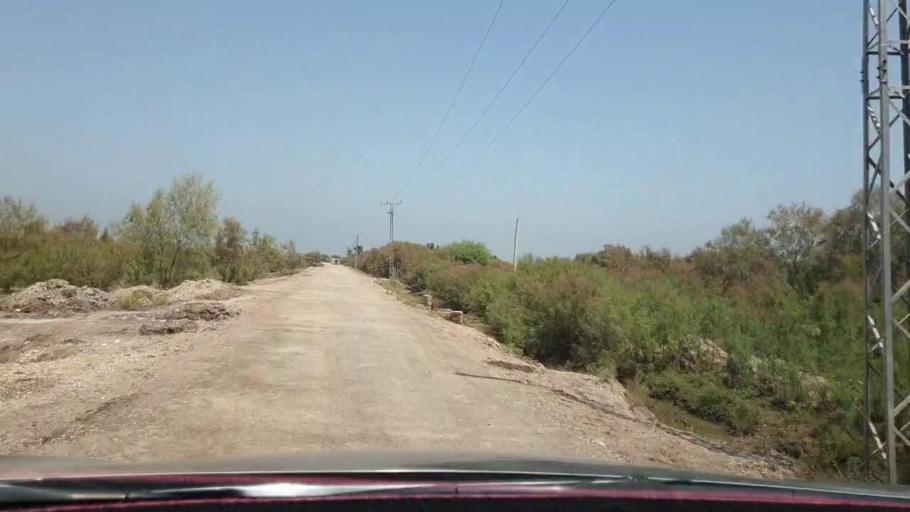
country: PK
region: Sindh
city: Warah
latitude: 27.4079
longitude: 67.6960
